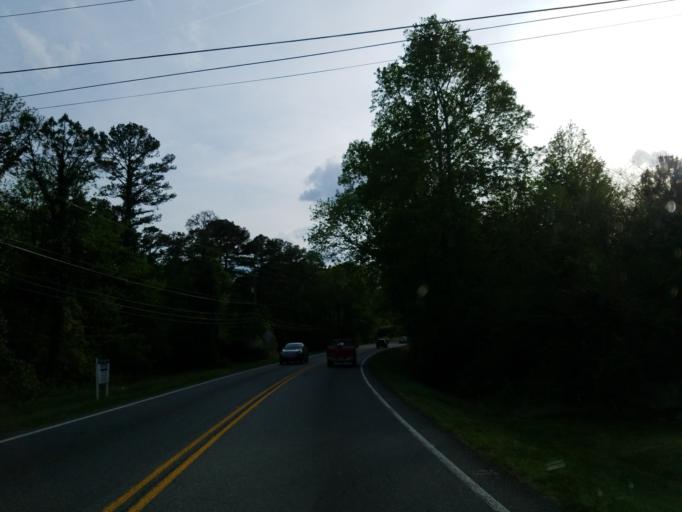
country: US
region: Georgia
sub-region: Cherokee County
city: Canton
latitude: 34.2388
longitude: -84.4305
